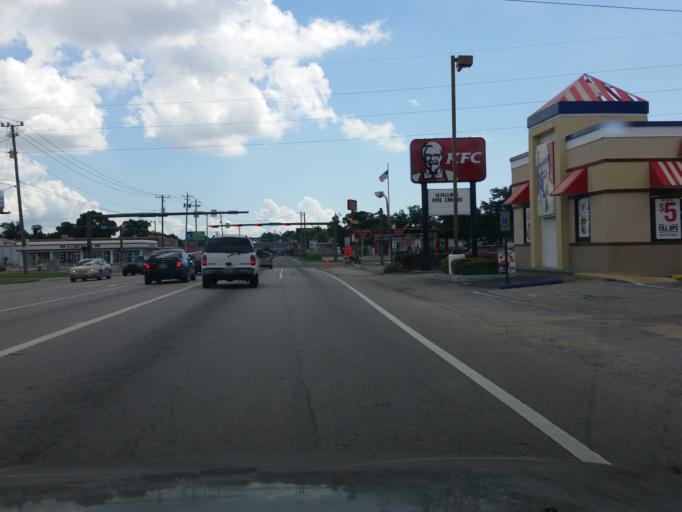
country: US
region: Florida
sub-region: Escambia County
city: Warrington
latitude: 30.3876
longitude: -87.2793
